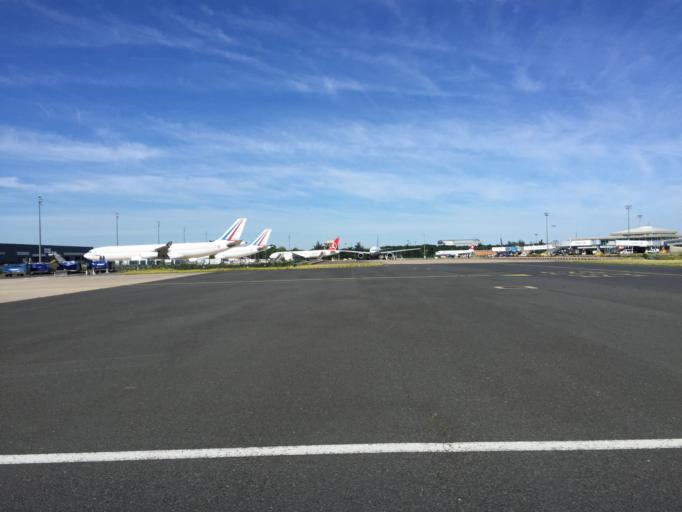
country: FR
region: Ile-de-France
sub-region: Departement du Val-d'Oise
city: Roissy-en-France
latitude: 49.0118
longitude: 2.5440
